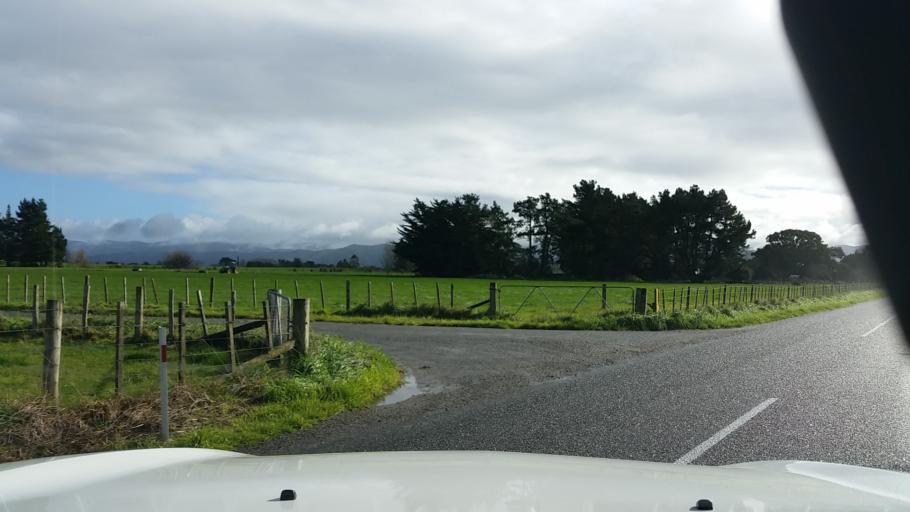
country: NZ
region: Wellington
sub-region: Masterton District
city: Masterton
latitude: -41.0335
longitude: 175.5435
